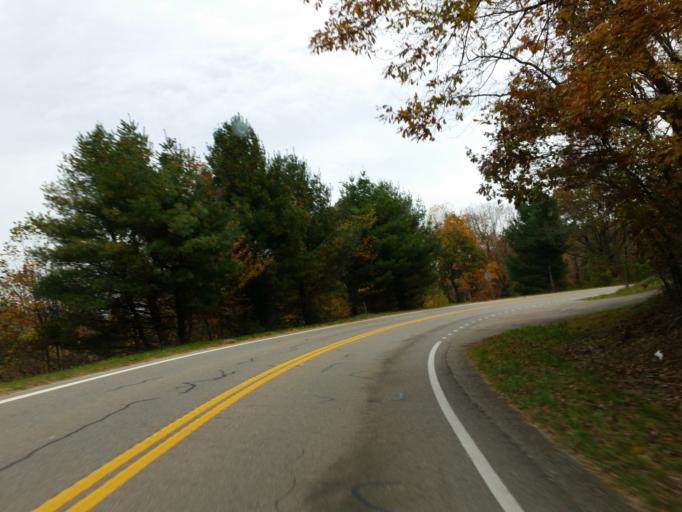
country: US
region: Georgia
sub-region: Pickens County
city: Jasper
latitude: 34.5436
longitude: -84.3701
